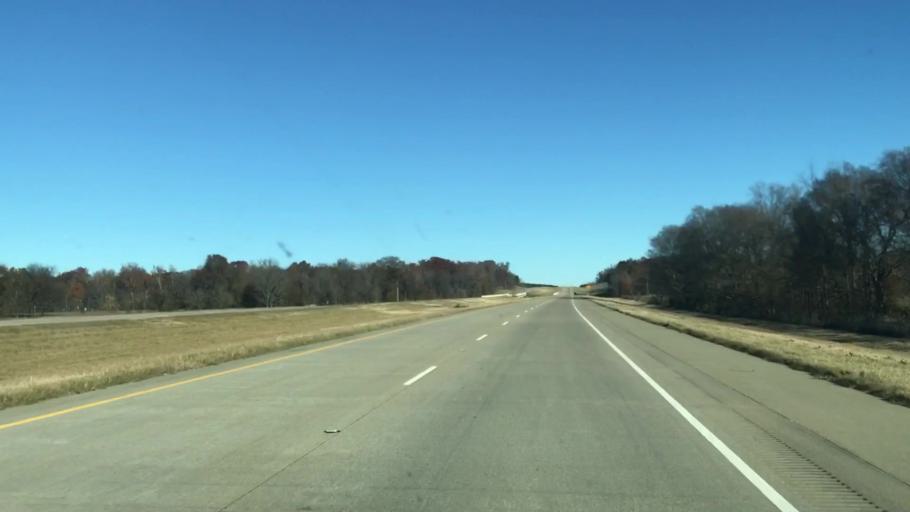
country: US
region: Louisiana
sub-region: Caddo Parish
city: Oil City
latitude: 32.7831
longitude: -93.8888
